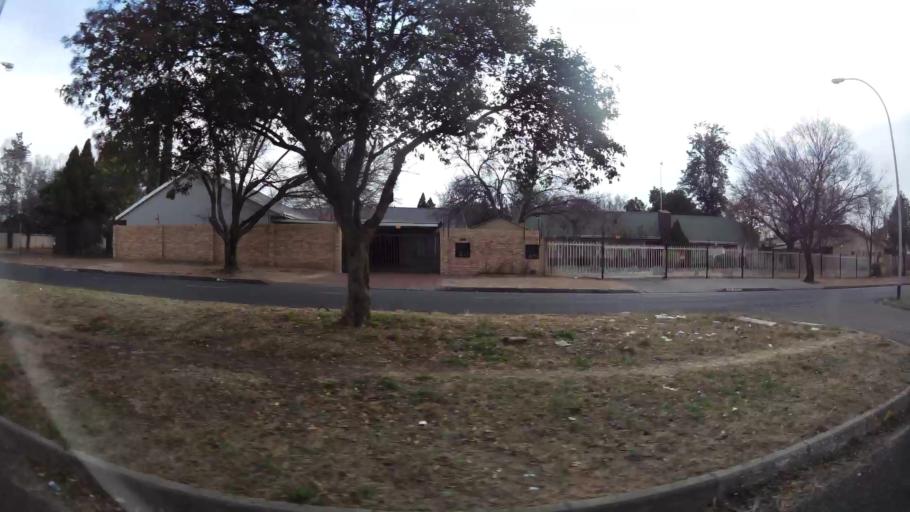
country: ZA
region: Orange Free State
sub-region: Mangaung Metropolitan Municipality
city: Bloemfontein
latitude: -29.1234
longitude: 26.1828
